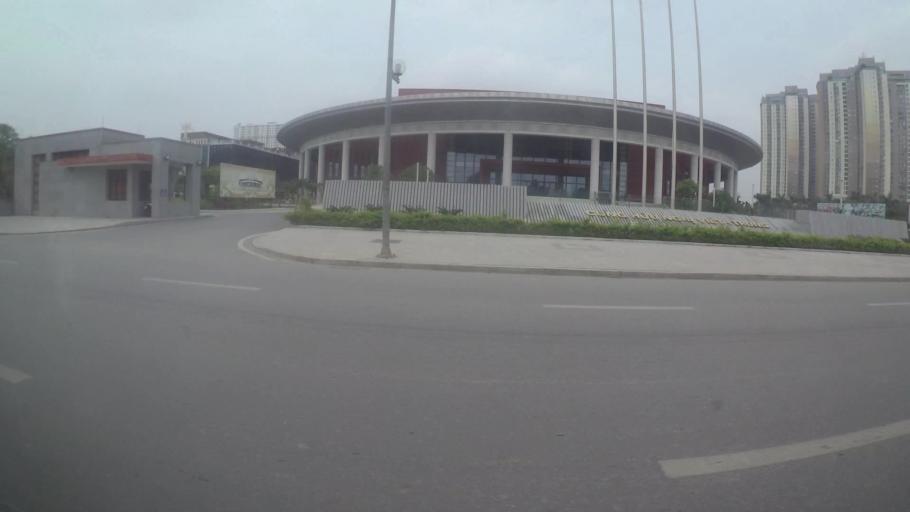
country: VN
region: Ha Noi
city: Cau Dien
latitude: 21.0123
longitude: 105.7711
